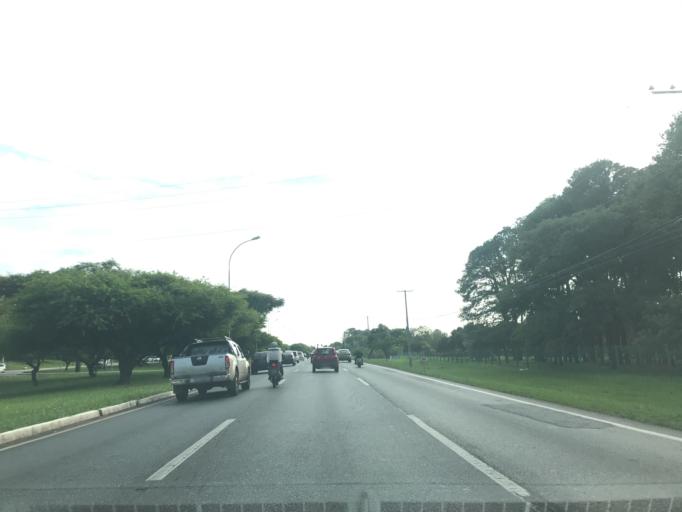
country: BR
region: Federal District
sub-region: Brasilia
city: Brasilia
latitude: -15.8050
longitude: -47.9247
